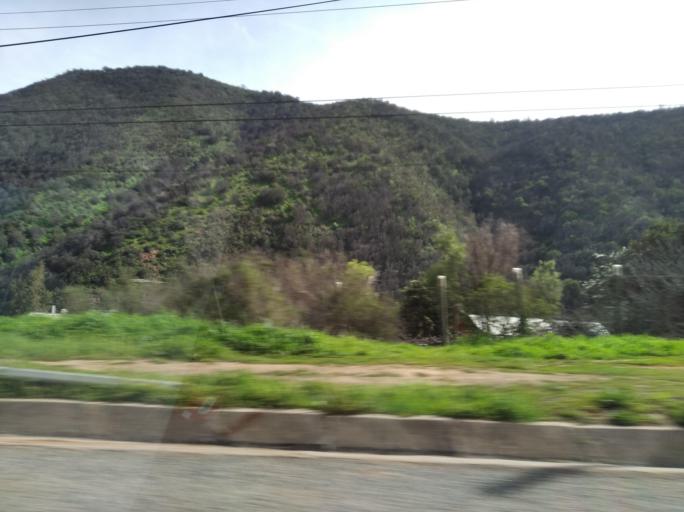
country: CL
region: Valparaiso
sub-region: Provincia de Marga Marga
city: Limache
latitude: -33.0615
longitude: -71.0599
